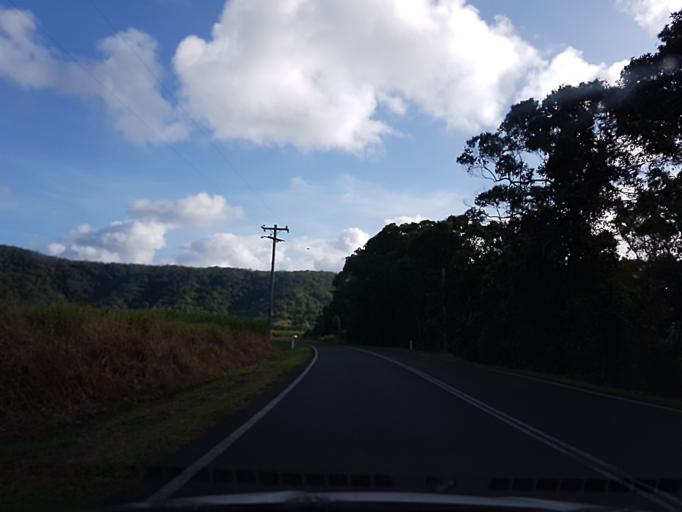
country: AU
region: Queensland
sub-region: Cairns
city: Port Douglas
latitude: -16.2778
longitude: 145.3844
